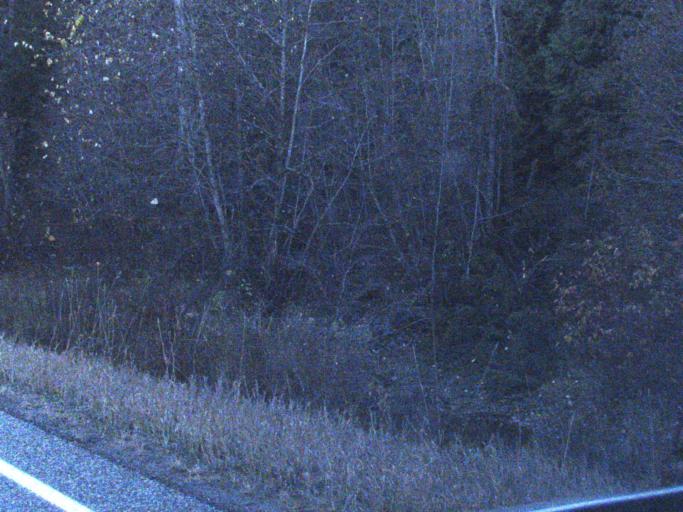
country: CA
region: British Columbia
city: Rossland
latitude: 48.9855
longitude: -117.8270
